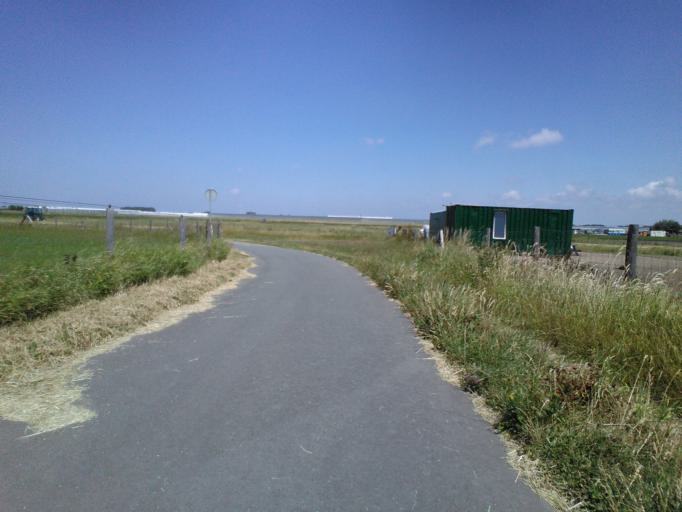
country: NL
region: South Holland
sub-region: Gemeente Westland
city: Maasdijk
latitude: 51.9442
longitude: 4.2019
